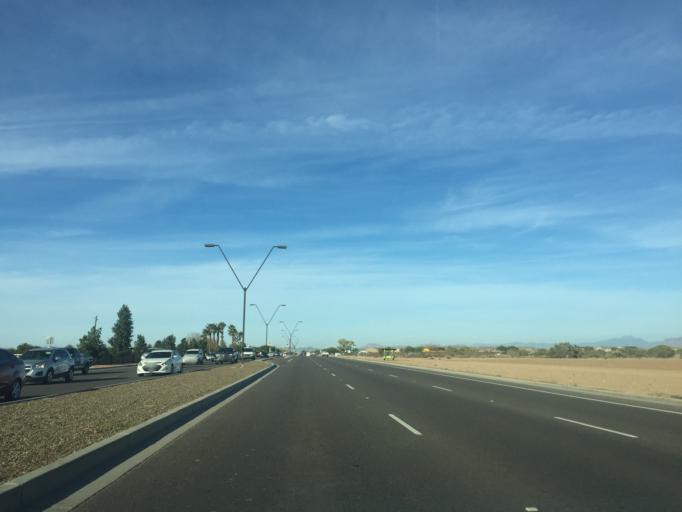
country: US
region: Arizona
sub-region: Maricopa County
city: Queen Creek
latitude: 33.2221
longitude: -111.6344
